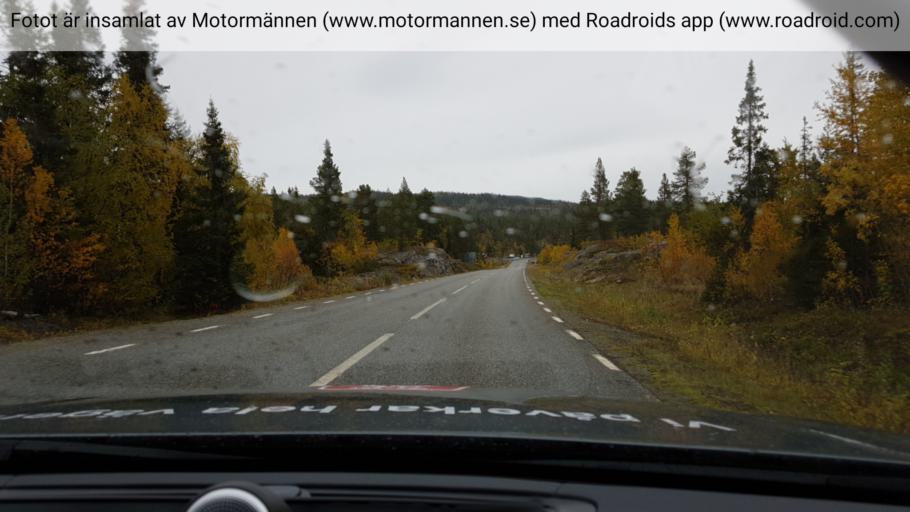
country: SE
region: Vaesterbotten
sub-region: Vilhelmina Kommun
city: Sjoberg
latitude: 64.9575
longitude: 15.4571
